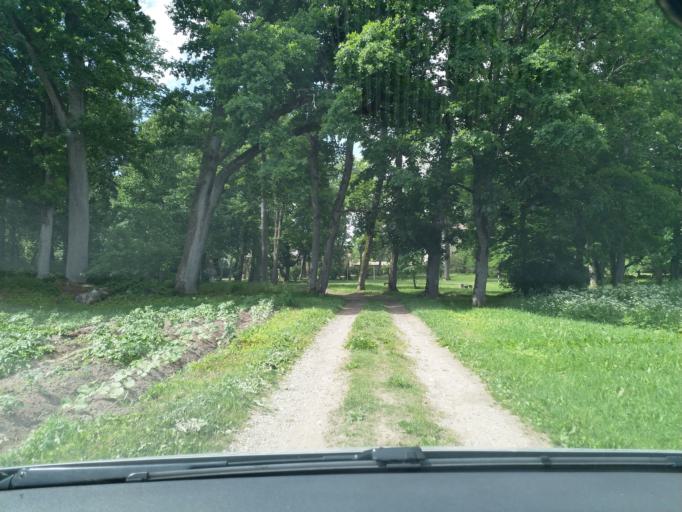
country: LV
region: Kuldigas Rajons
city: Kuldiga
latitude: 56.8390
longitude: 21.9466
